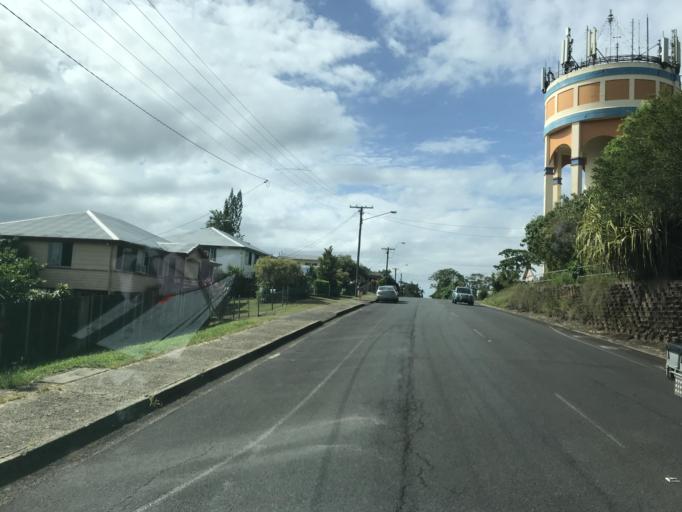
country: AU
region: Queensland
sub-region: Cassowary Coast
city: Innisfail
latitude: -17.5279
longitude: 146.0344
